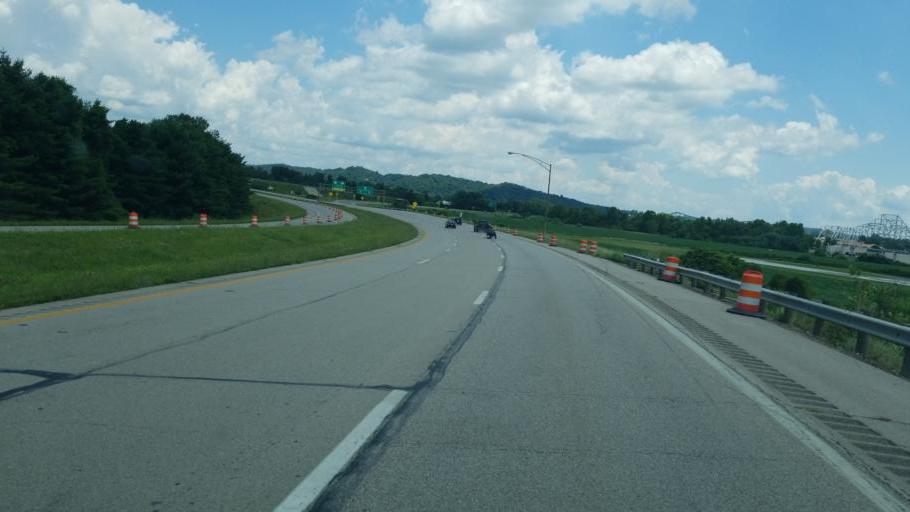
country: US
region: West Virginia
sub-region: Mason County
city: Point Pleasant
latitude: 38.8378
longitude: -82.1616
